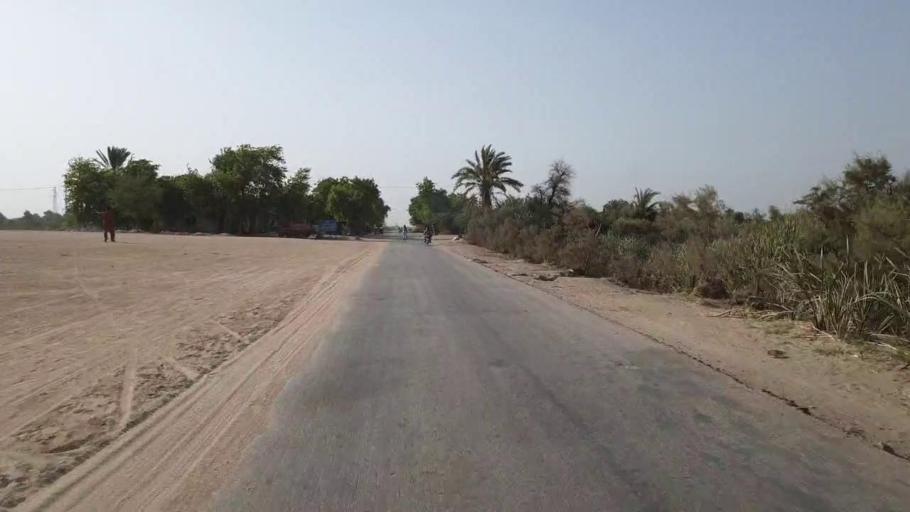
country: PK
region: Sindh
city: Khadro
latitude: 26.3363
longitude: 68.9278
